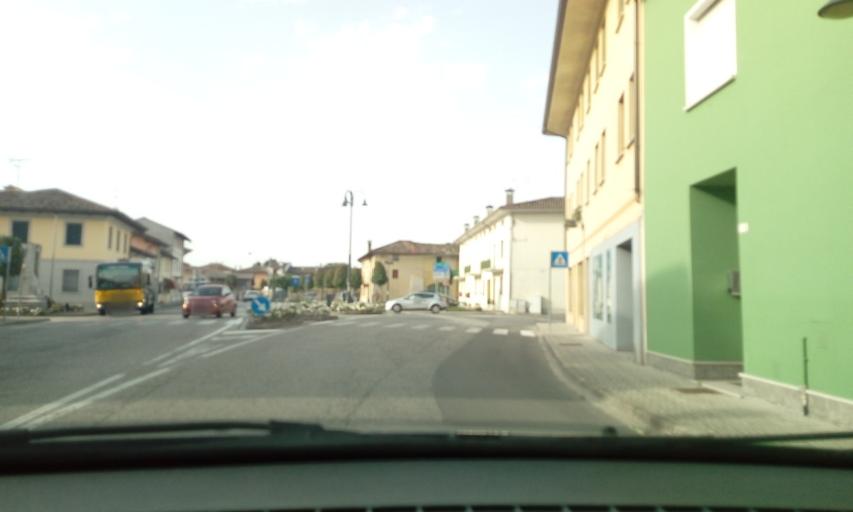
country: IT
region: Friuli Venezia Giulia
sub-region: Provincia di Udine
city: Ialmicco
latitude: 45.9125
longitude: 13.3457
